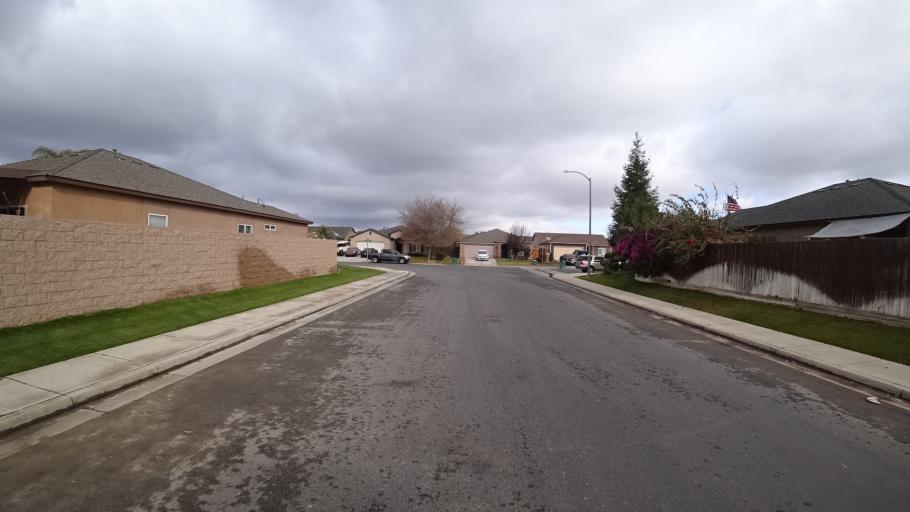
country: US
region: California
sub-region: Kern County
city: Greenfield
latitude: 35.2942
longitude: -119.0011
